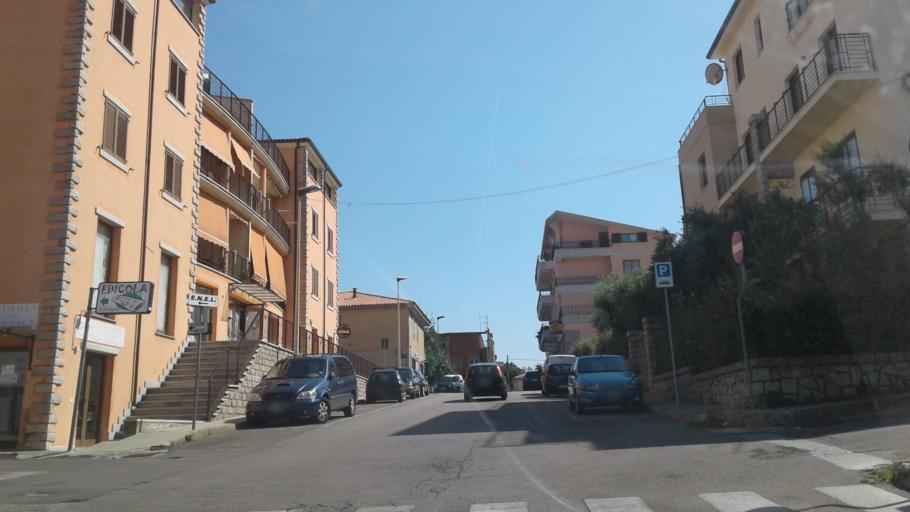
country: IT
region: Sardinia
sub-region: Provincia di Olbia-Tempio
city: Tempio Pausania
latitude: 40.8978
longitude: 9.1080
